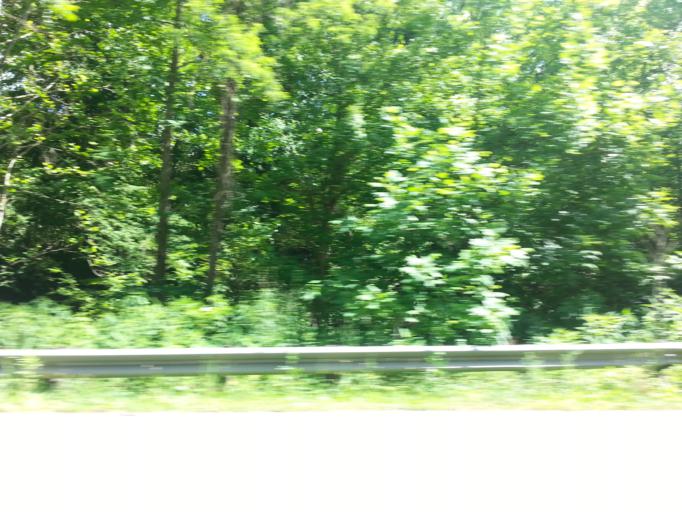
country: US
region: Virginia
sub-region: Lee County
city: Pennington Gap
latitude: 36.7668
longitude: -83.1023
